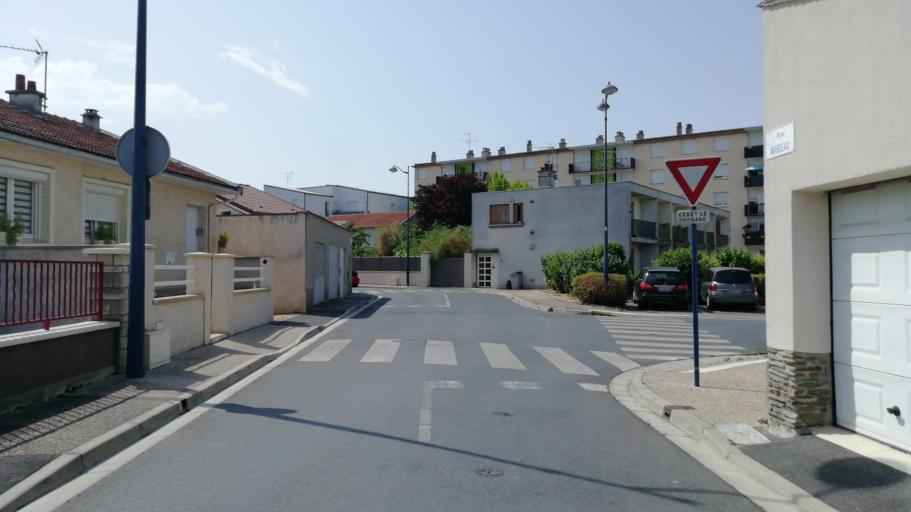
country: FR
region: Champagne-Ardenne
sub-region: Departement de la Marne
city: Betheny
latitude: 49.2715
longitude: 4.0475
